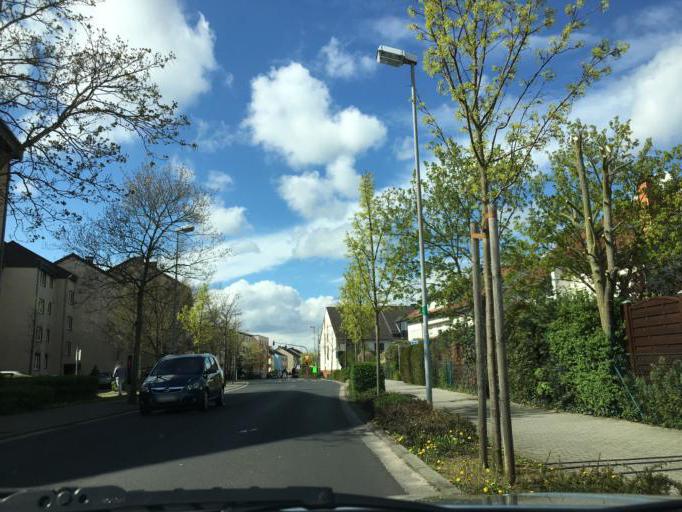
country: DE
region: Hesse
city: Obertshausen
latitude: 50.0664
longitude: 8.8453
